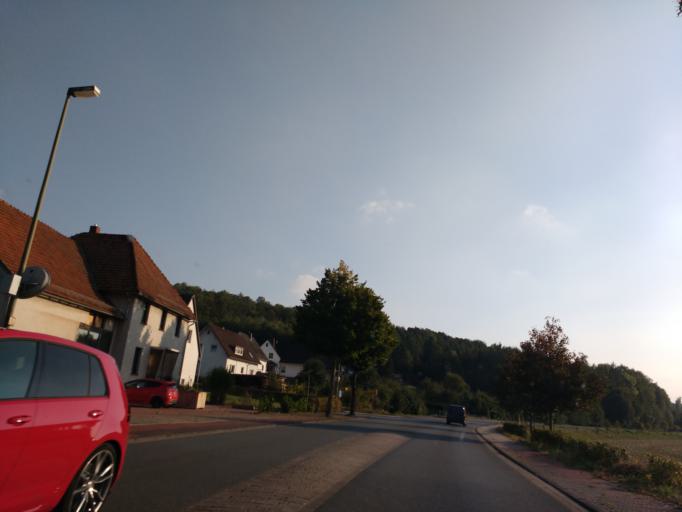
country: DE
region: North Rhine-Westphalia
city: Brakel
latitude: 51.6760
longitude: 9.1641
